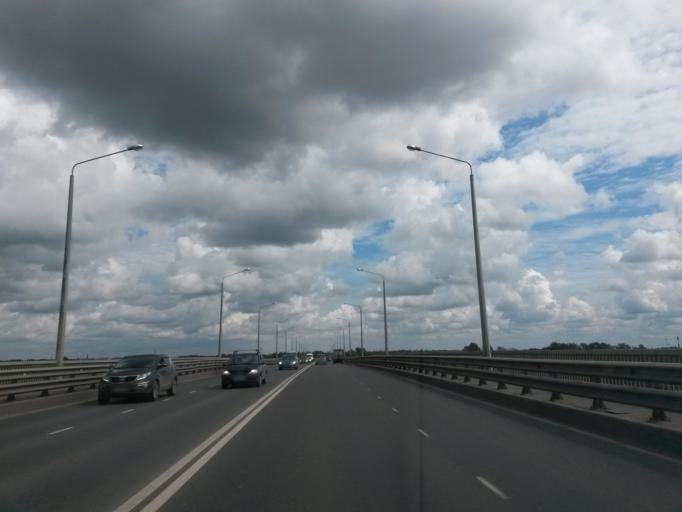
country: RU
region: Jaroslavl
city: Yaroslavl
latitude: 57.6405
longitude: 39.8927
